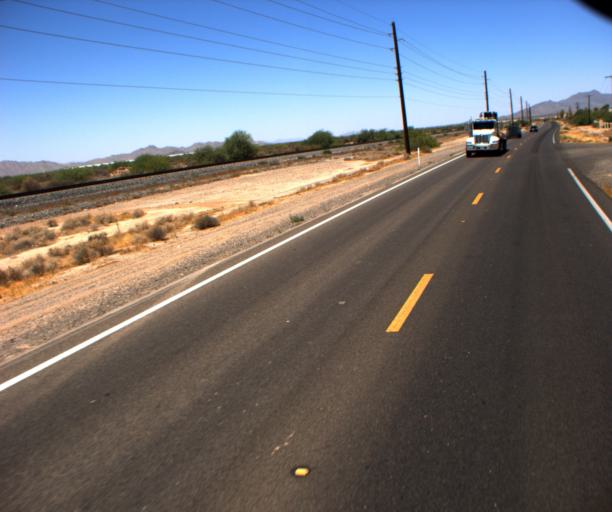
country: US
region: Arizona
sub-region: Pinal County
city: Maricopa
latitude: 33.0730
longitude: -112.0803
